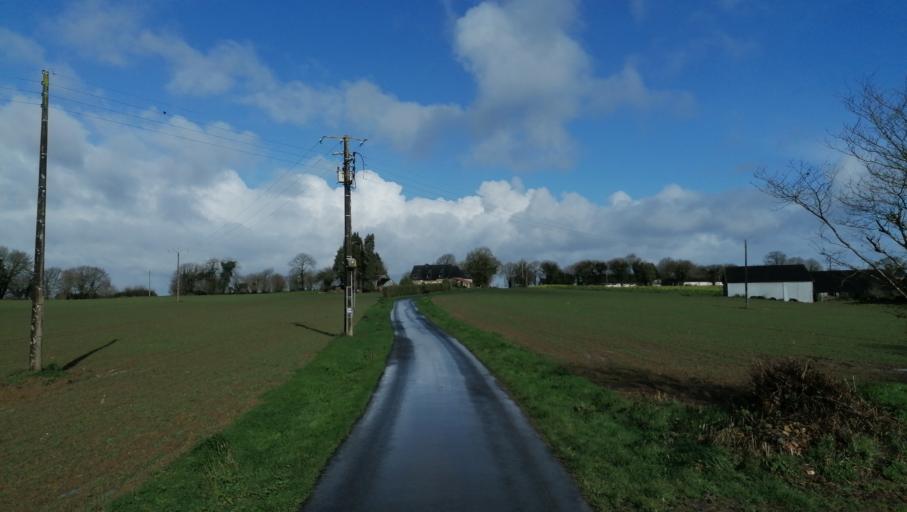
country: FR
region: Brittany
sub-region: Departement des Cotes-d'Armor
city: Lanrodec
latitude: 48.4845
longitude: -3.0199
